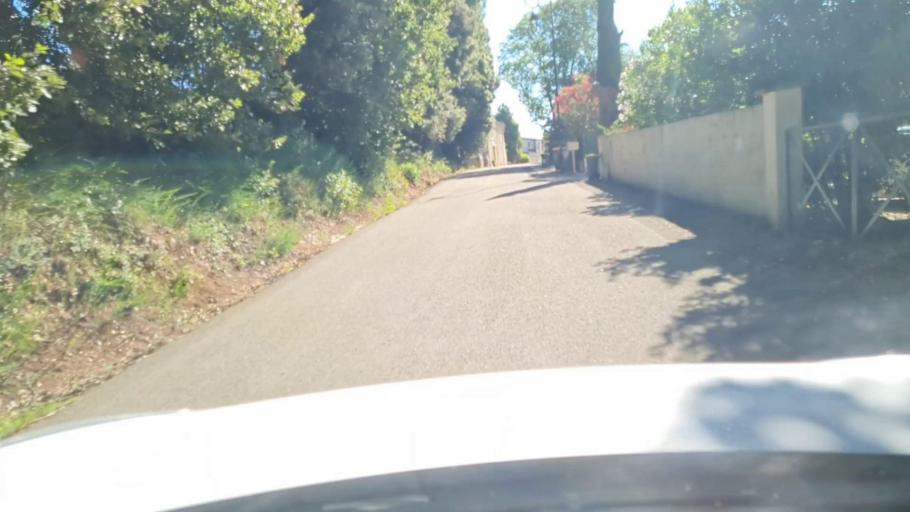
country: FR
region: Languedoc-Roussillon
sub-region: Departement du Gard
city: Sommieres
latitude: 43.8093
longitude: 4.0452
